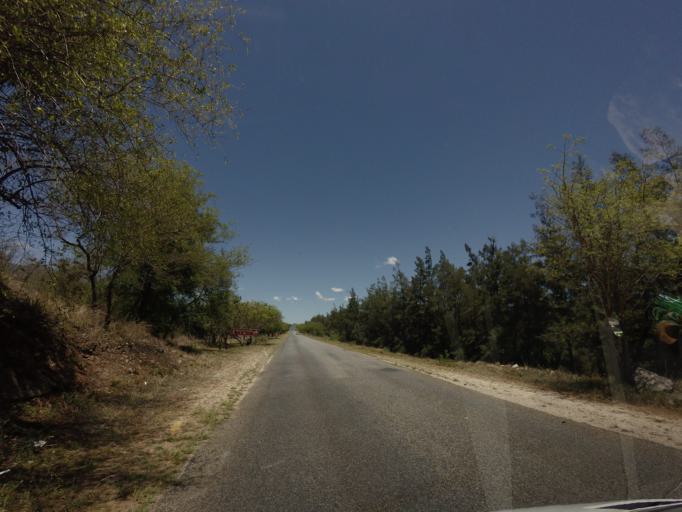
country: ZA
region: Limpopo
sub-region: Mopani District Municipality
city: Hoedspruit
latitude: -24.3732
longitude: 30.7092
